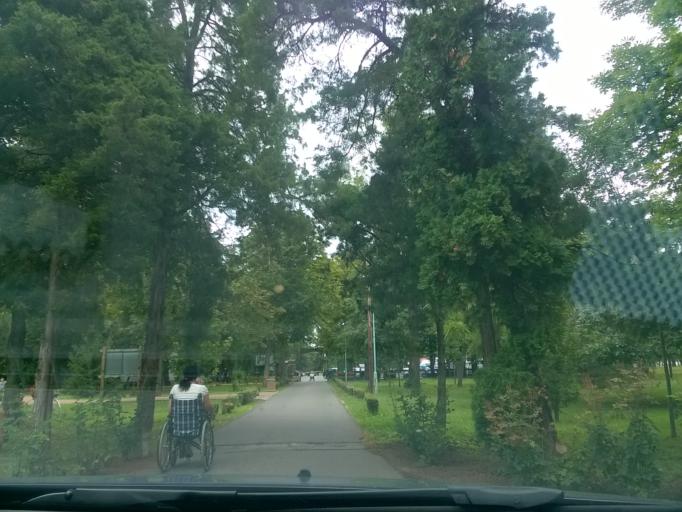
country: RS
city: Melenci
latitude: 45.5274
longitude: 20.3040
